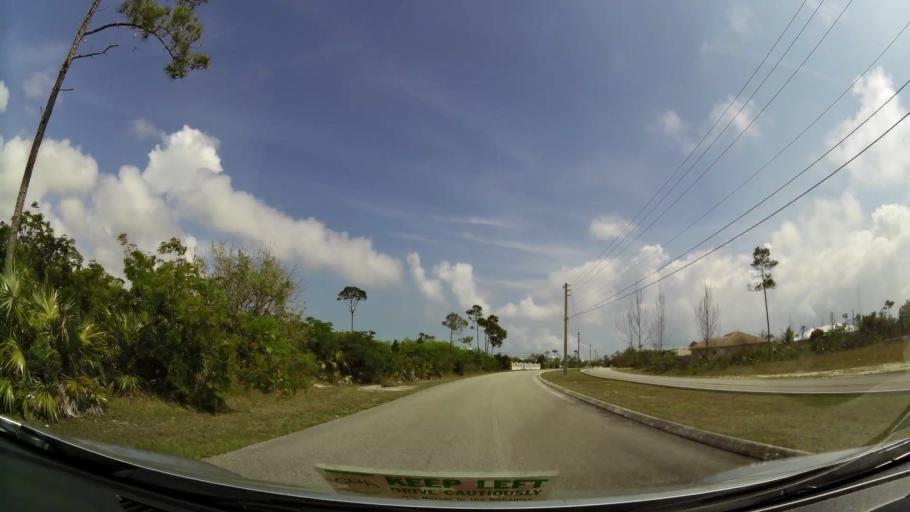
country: BS
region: Freeport
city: Freeport
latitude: 26.5050
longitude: -78.7168
